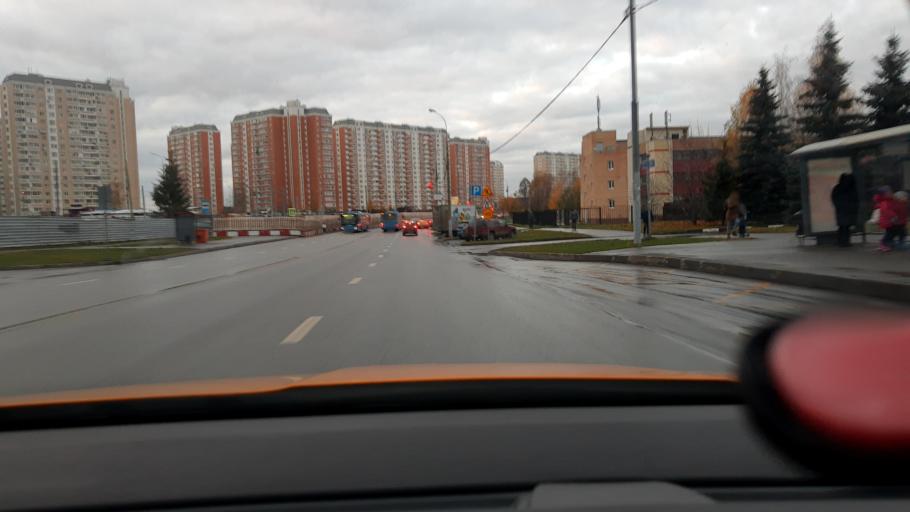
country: RU
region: Moscow
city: Novo-Peredelkino
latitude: 55.6396
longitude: 37.3338
